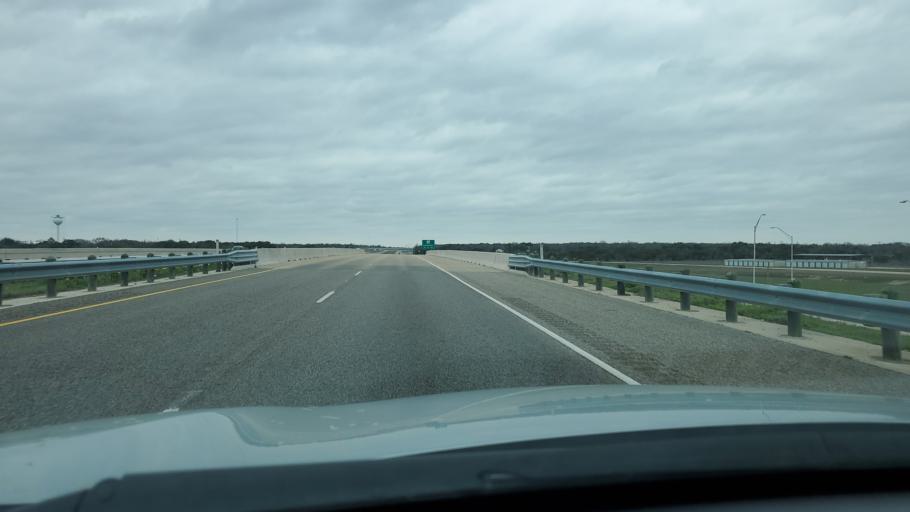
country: US
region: Texas
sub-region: Williamson County
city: Florence
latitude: 30.8432
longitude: -97.7853
